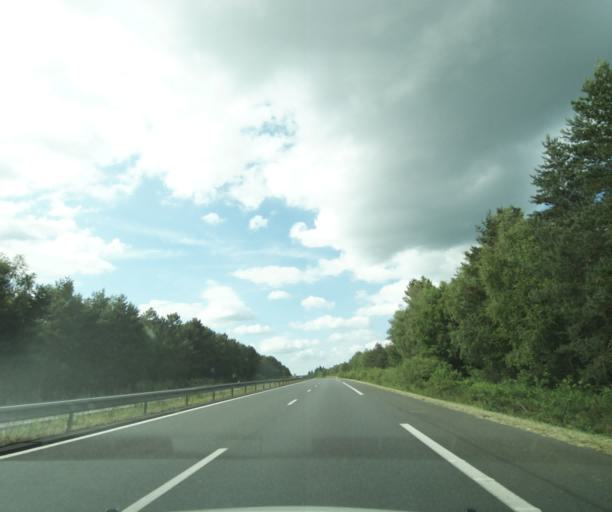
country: FR
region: Centre
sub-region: Departement du Loir-et-Cher
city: Chaumont-sur-Tharonne
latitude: 47.6221
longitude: 1.9613
